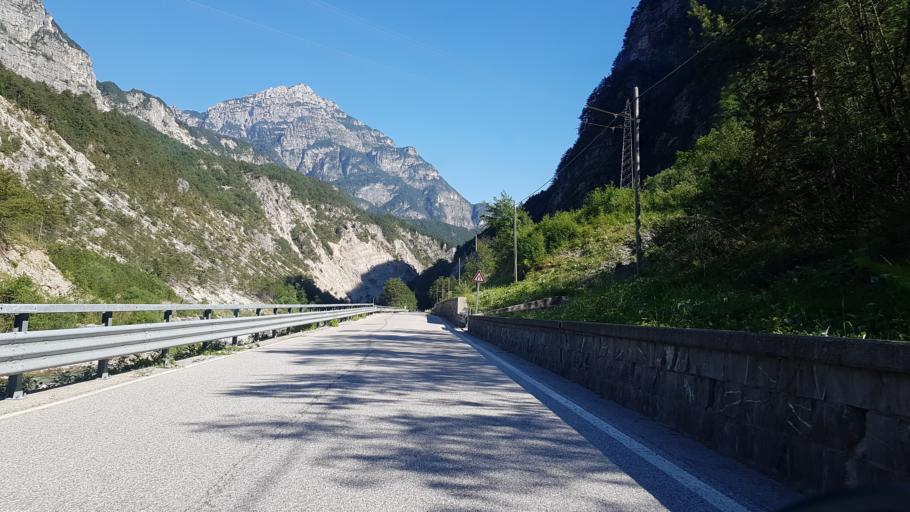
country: IT
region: Friuli Venezia Giulia
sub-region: Provincia di Udine
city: Moggio Udinese
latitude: 46.4475
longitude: 13.1876
